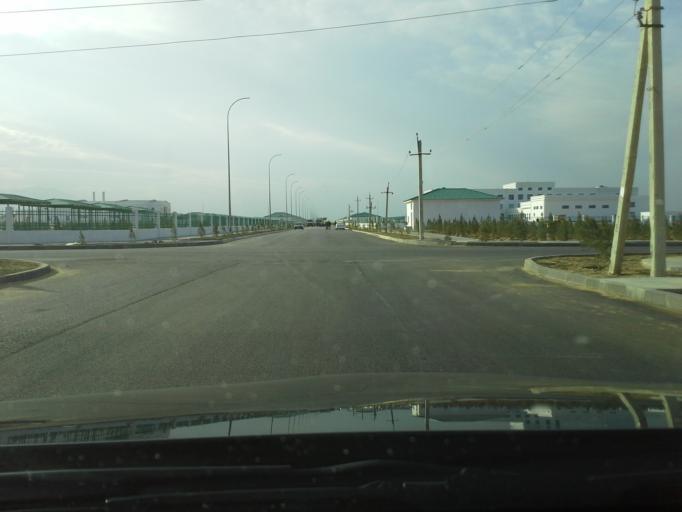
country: TM
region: Ahal
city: Abadan
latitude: 38.0968
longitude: 58.3125
